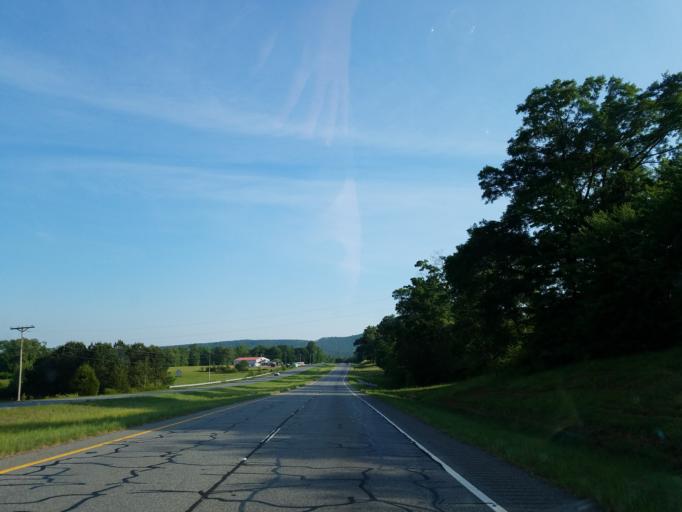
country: US
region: Georgia
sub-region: Chattooga County
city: Summerville
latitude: 34.4361
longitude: -85.2486
